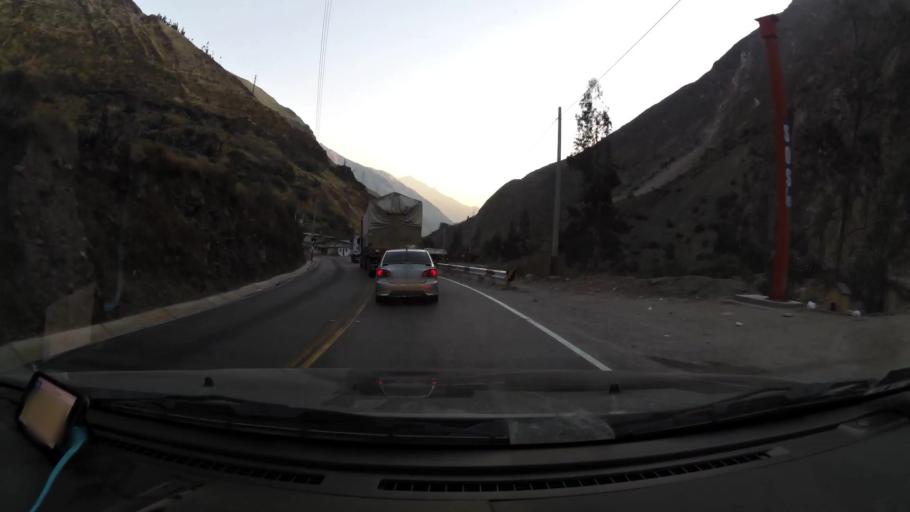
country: PE
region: Lima
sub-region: Provincia de Huarochiri
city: Matucana
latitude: -11.8154
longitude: -76.3572
